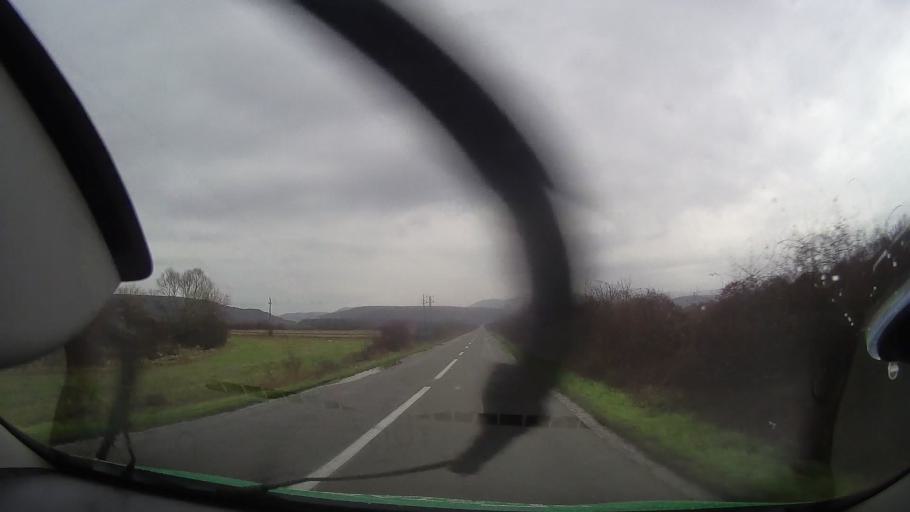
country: RO
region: Bihor
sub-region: Comuna Soimi
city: Soimi
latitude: 46.6944
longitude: 22.0956
